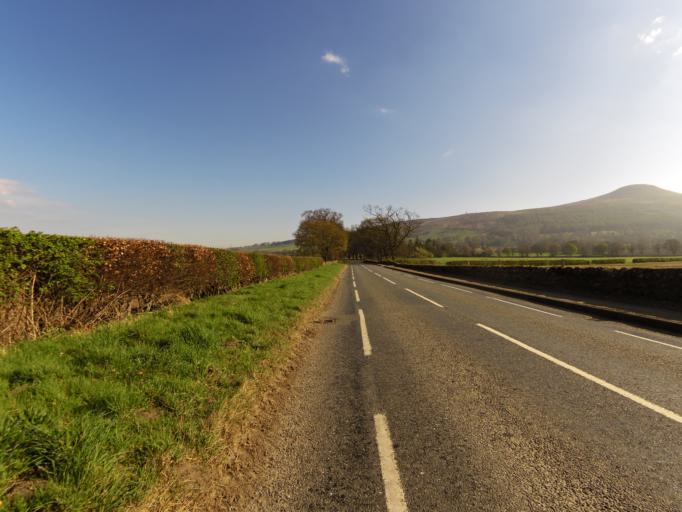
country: GB
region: Scotland
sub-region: Fife
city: Falkland
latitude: 56.2610
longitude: -3.2076
